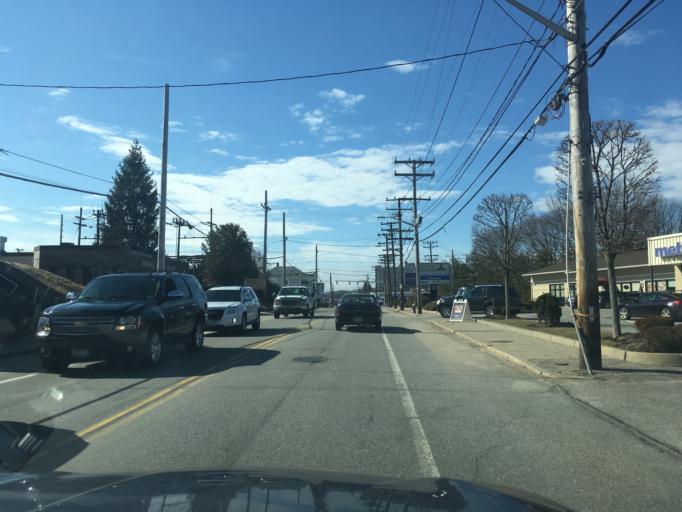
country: US
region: Rhode Island
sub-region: Providence County
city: Cranston
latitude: 41.7838
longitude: -71.4591
